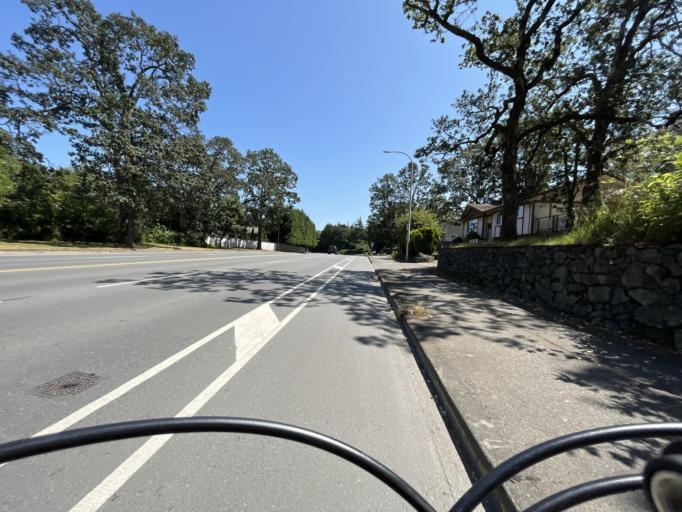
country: CA
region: British Columbia
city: Oak Bay
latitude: 48.4697
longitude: -123.3423
